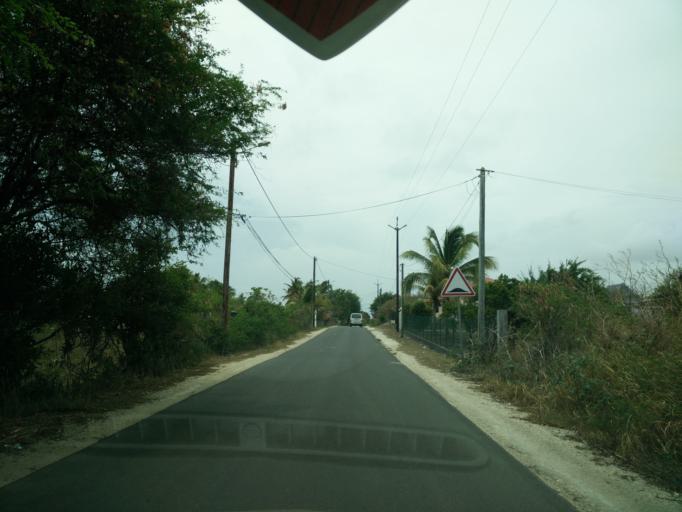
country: GP
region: Guadeloupe
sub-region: Guadeloupe
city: Le Moule
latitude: 16.3235
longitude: -61.3057
